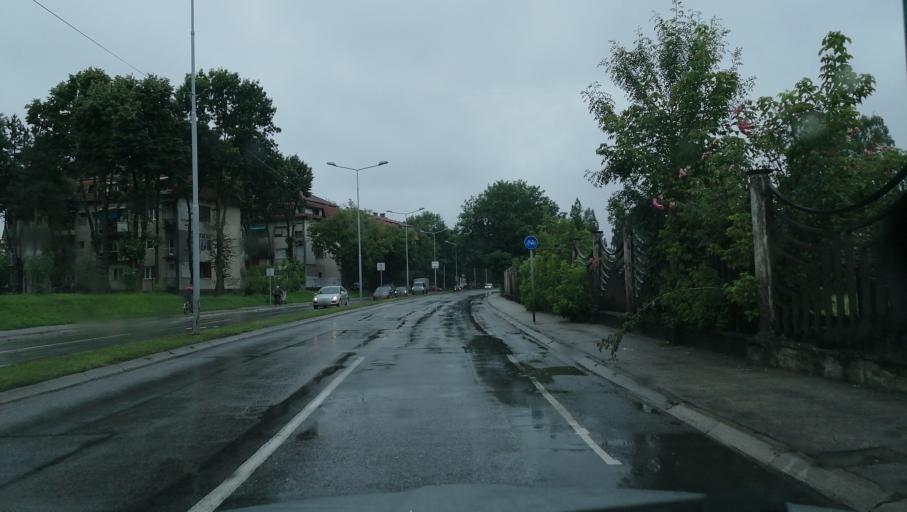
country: RS
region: Central Serbia
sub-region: Raski Okrug
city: Kraljevo
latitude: 43.7285
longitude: 20.6861
